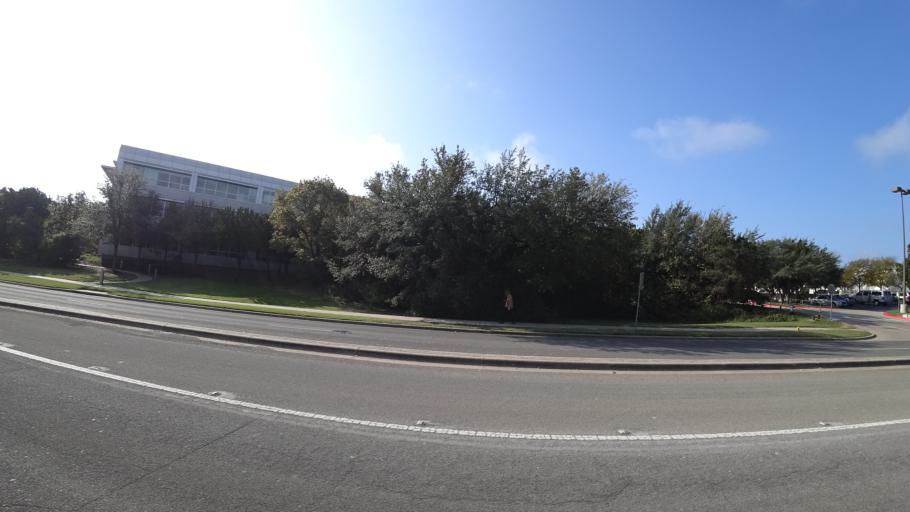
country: US
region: Texas
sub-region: Williamson County
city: Anderson Mill
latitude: 30.4056
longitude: -97.8498
